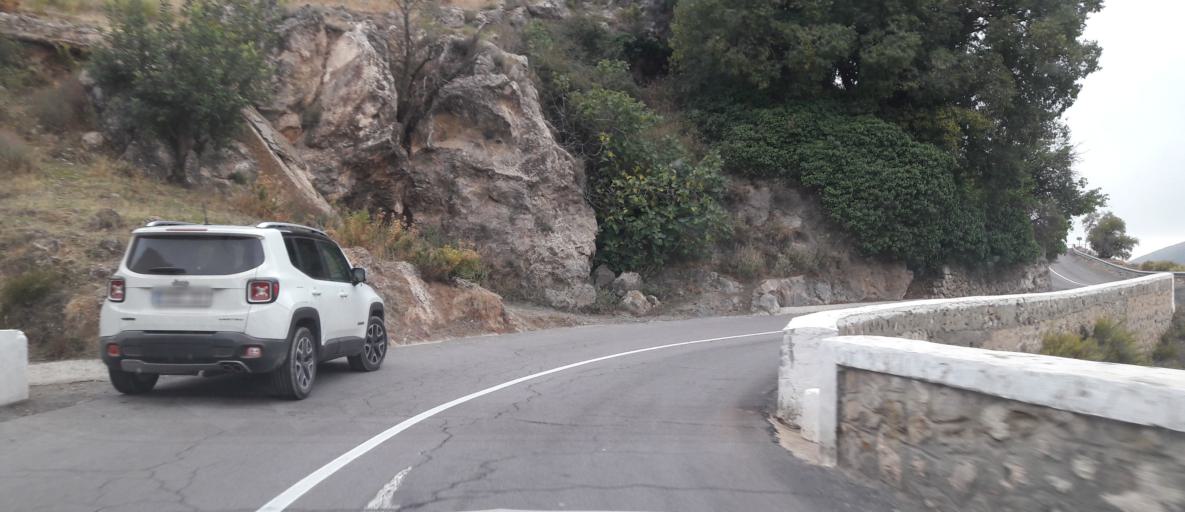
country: ES
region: Andalusia
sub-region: Provincia de Almeria
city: Enix
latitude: 36.8874
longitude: -2.6247
